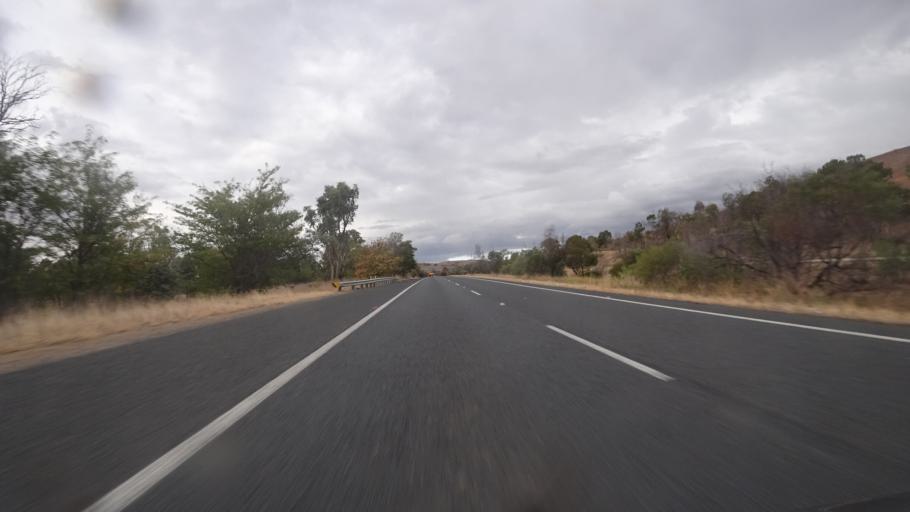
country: AU
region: New South Wales
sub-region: Yass Valley
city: Yass
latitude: -34.7884
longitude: 148.7002
